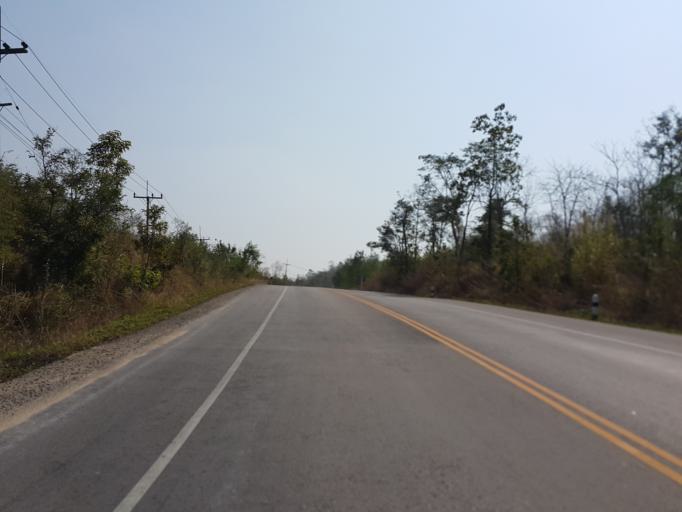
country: TH
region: Lampang
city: Mueang Pan
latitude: 18.8849
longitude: 99.6026
